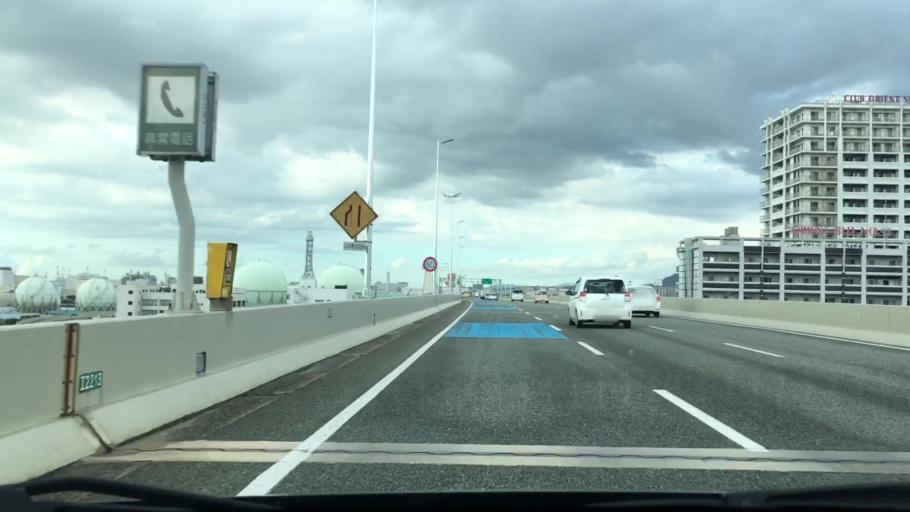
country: JP
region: Fukuoka
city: Fukuoka-shi
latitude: 33.6122
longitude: 130.4097
